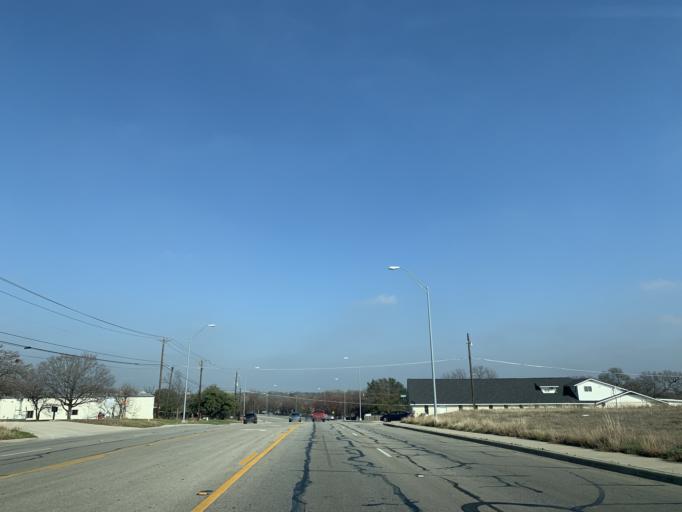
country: US
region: Texas
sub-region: Williamson County
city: Round Rock
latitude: 30.5266
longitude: -97.6531
